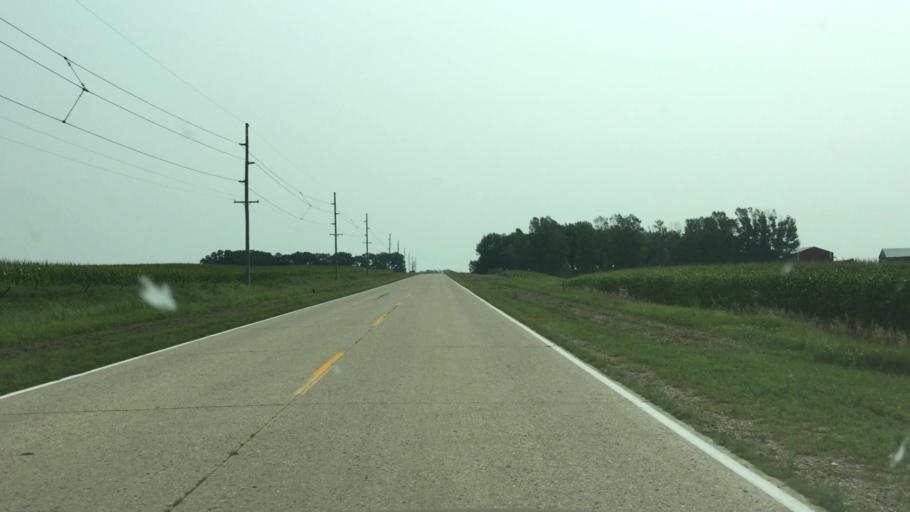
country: US
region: Iowa
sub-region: Dickinson County
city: Milford
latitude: 43.3714
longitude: -95.2002
